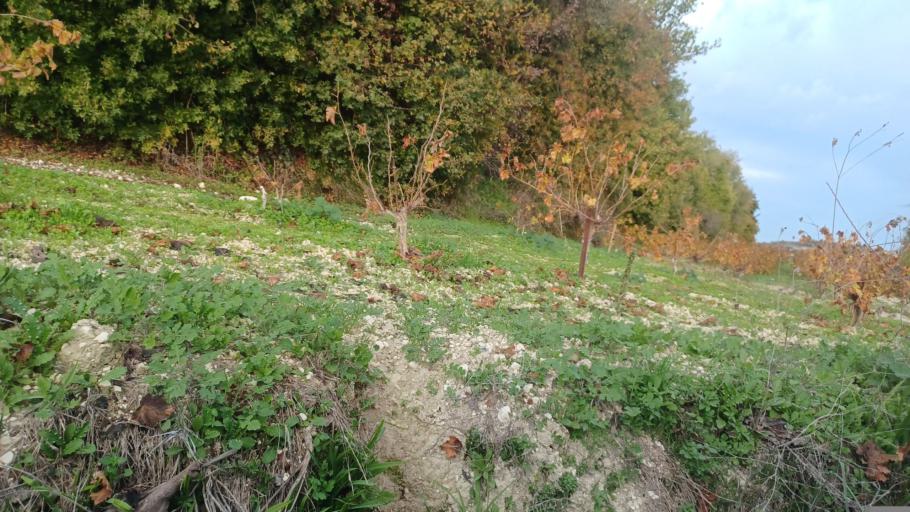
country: CY
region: Pafos
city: Mesogi
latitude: 34.8644
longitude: 32.5148
